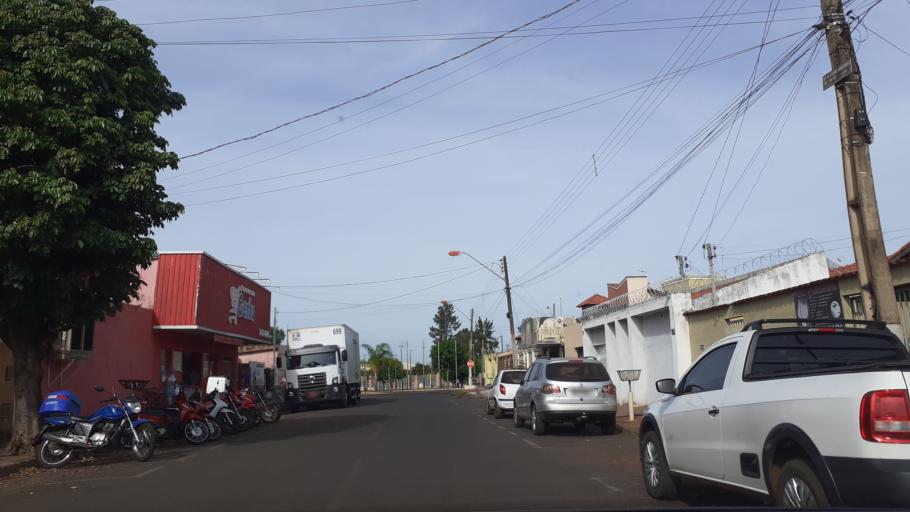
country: BR
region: Goias
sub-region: Itumbiara
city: Itumbiara
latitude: -18.4219
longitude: -49.2468
